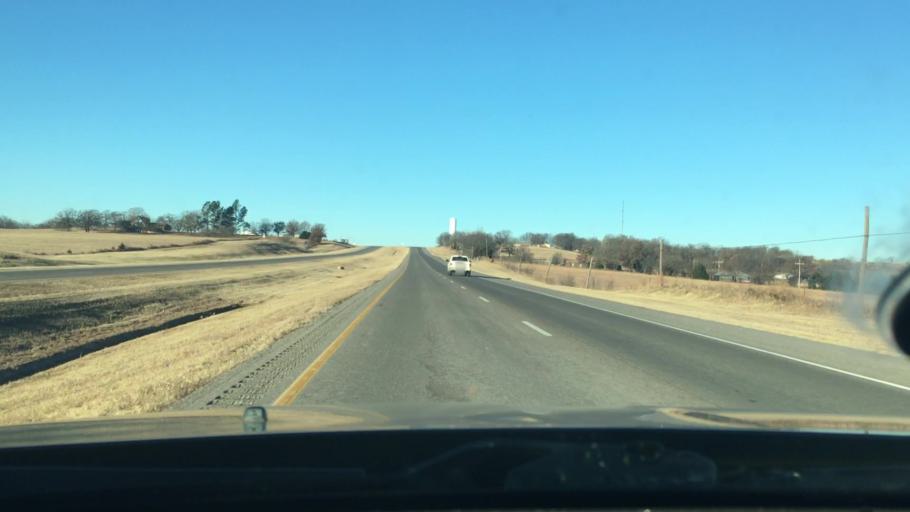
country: US
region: Oklahoma
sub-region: Murray County
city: Sulphur
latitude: 34.5064
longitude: -97.0384
